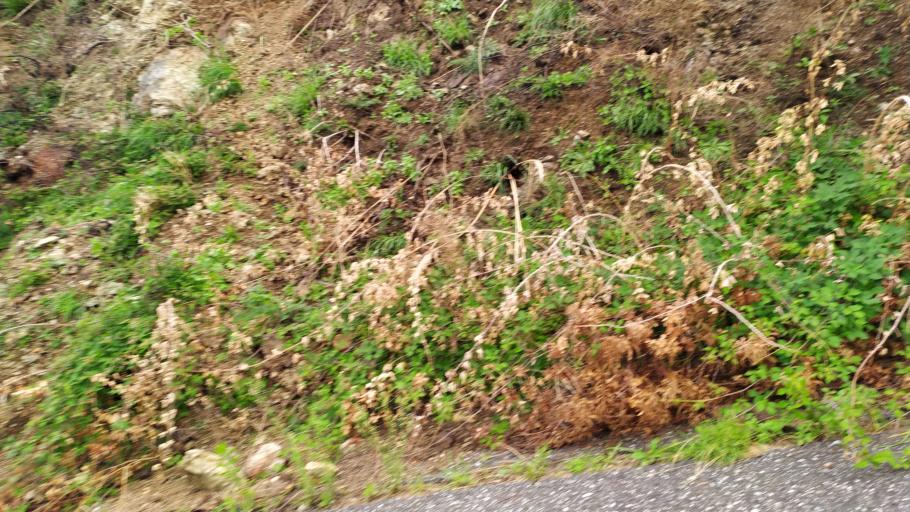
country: IT
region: Sicily
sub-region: Messina
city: Villafranca Tirrena
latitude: 38.2193
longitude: 15.4691
